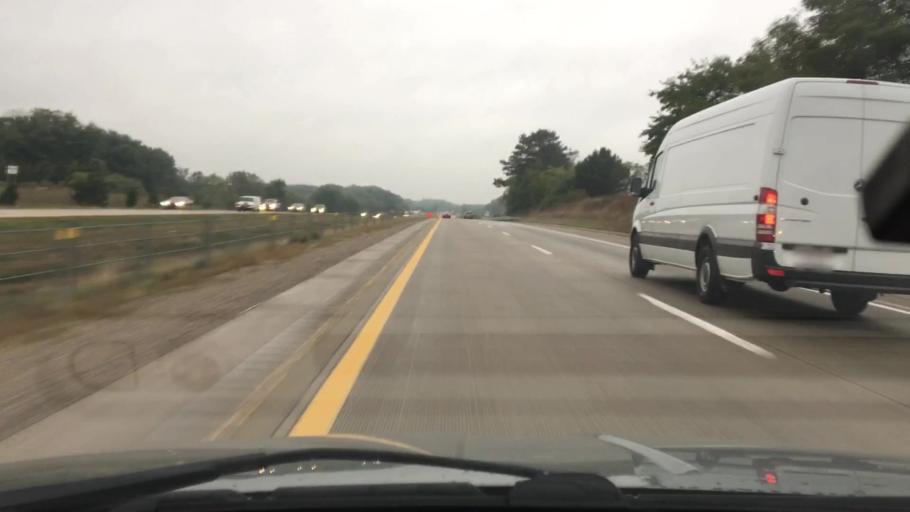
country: US
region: Michigan
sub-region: Jackson County
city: Grass Lake
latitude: 42.2921
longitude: -84.2450
